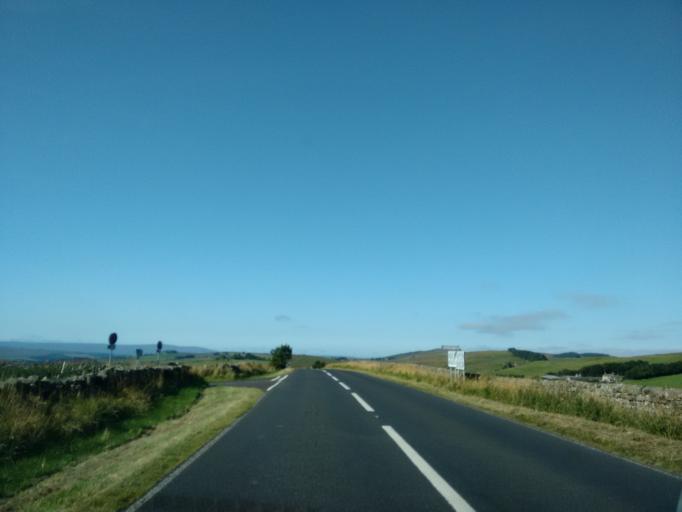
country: GB
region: England
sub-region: Northumberland
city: Bardon Mill
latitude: 55.0050
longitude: -2.3428
